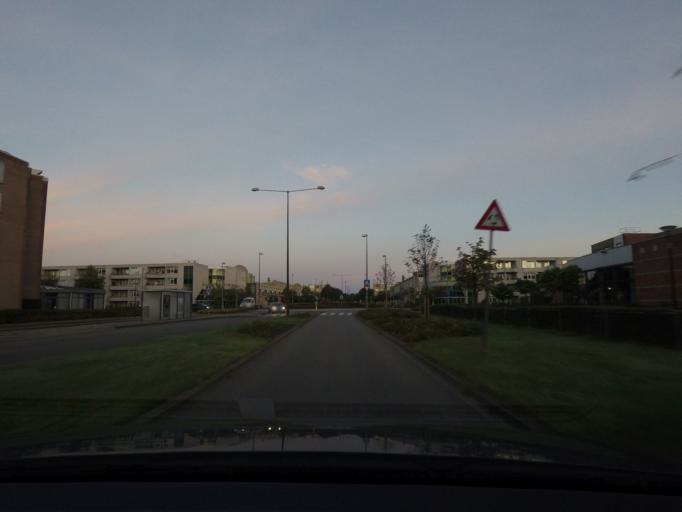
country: NL
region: North Holland
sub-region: Gemeente Alkmaar
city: Alkmaar
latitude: 52.6580
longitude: 4.7580
